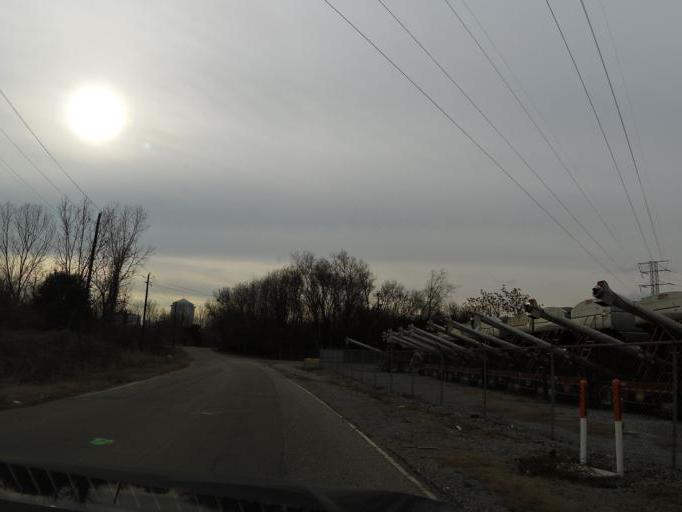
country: US
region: Alabama
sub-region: Montgomery County
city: Montgomery
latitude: 32.3911
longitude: -86.3134
